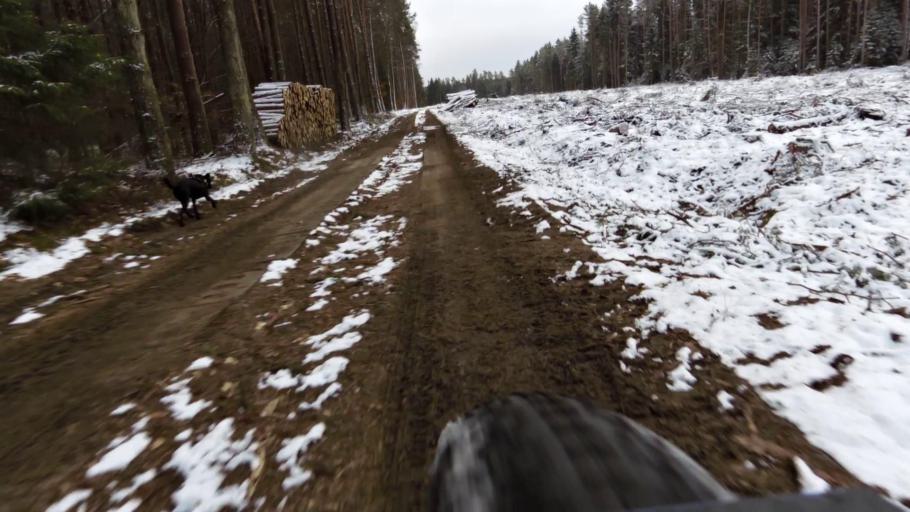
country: PL
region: West Pomeranian Voivodeship
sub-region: Powiat walecki
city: Miroslawiec
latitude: 53.3751
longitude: 16.1479
